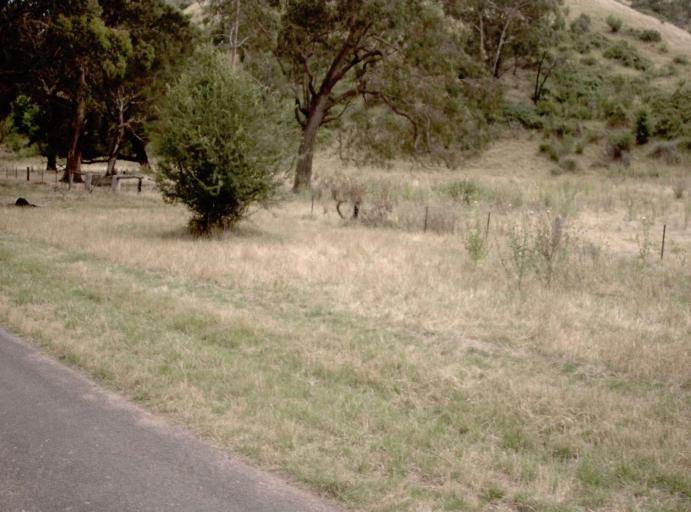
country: AU
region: Victoria
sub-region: Wellington
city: Heyfield
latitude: -37.6387
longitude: 146.6339
